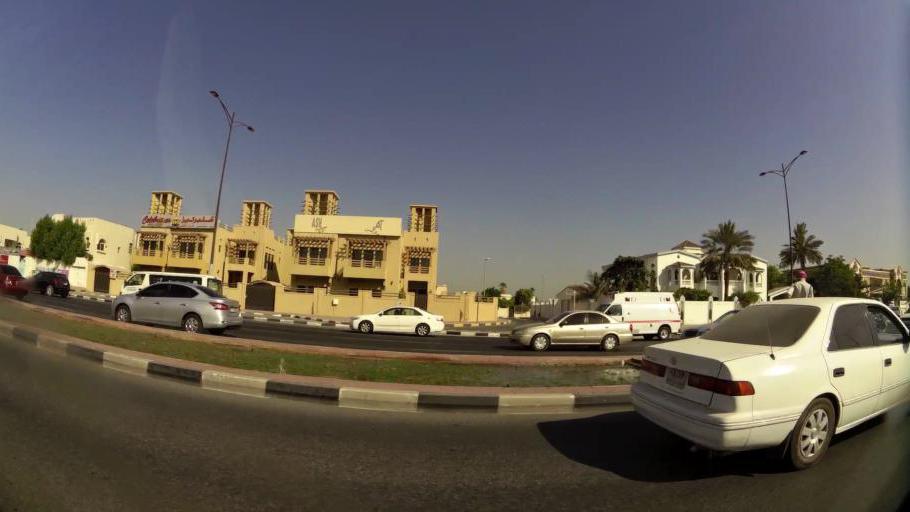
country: AE
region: Ash Shariqah
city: Sharjah
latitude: 25.3560
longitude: 55.4398
